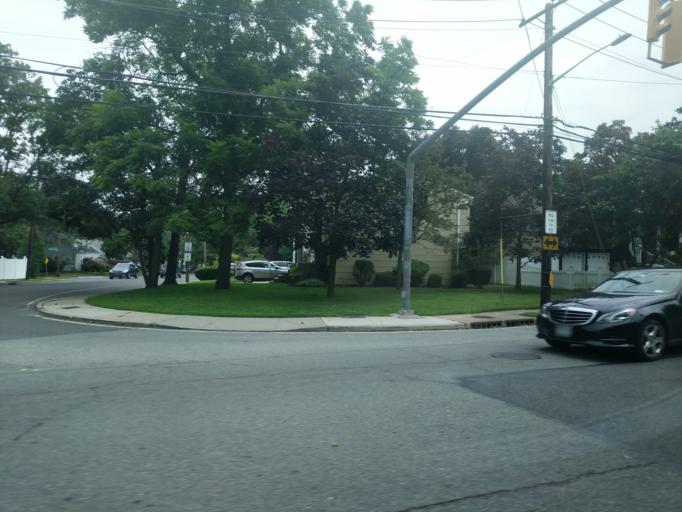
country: US
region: New York
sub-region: Nassau County
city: Hewlett Harbor
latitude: 40.6403
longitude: -73.6846
